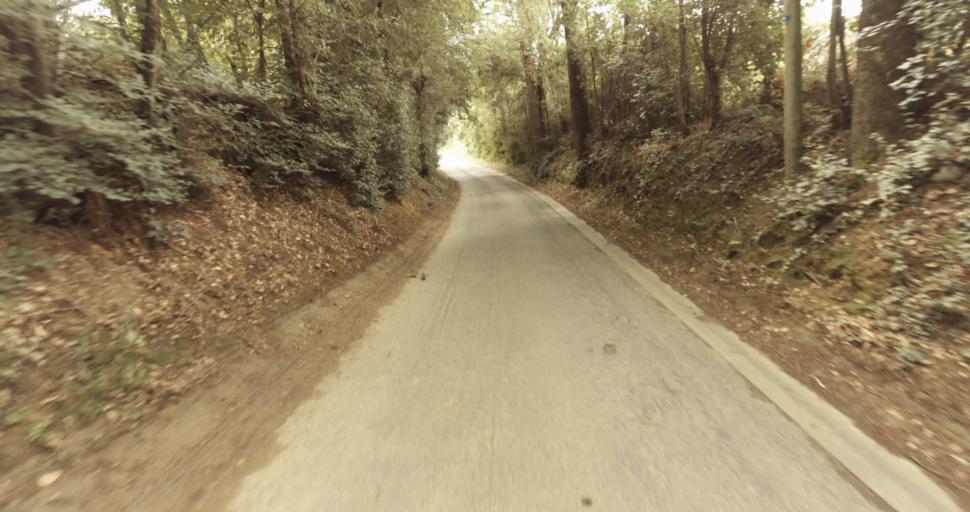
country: FR
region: Midi-Pyrenees
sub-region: Departement de la Haute-Garonne
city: Fontenilles
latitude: 43.5567
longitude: 1.2103
